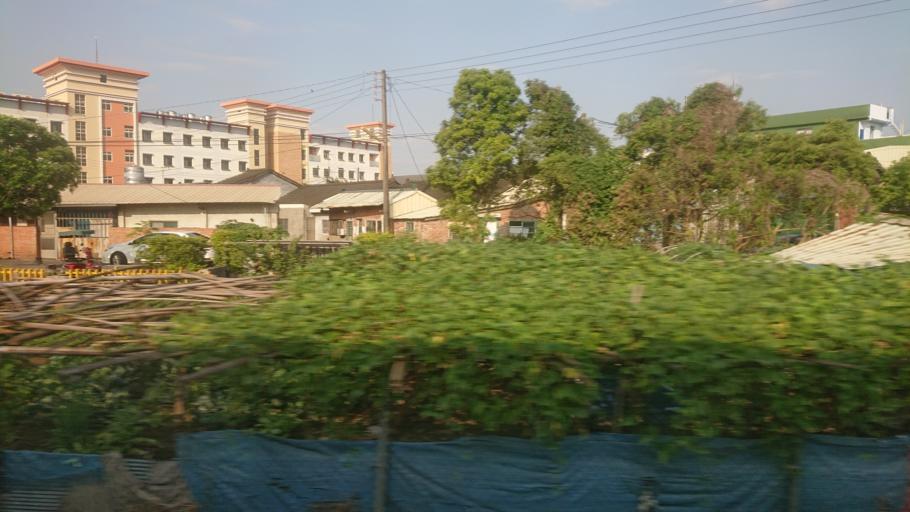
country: TW
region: Taiwan
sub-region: Chiayi
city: Jiayi Shi
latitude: 23.6048
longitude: 120.4592
